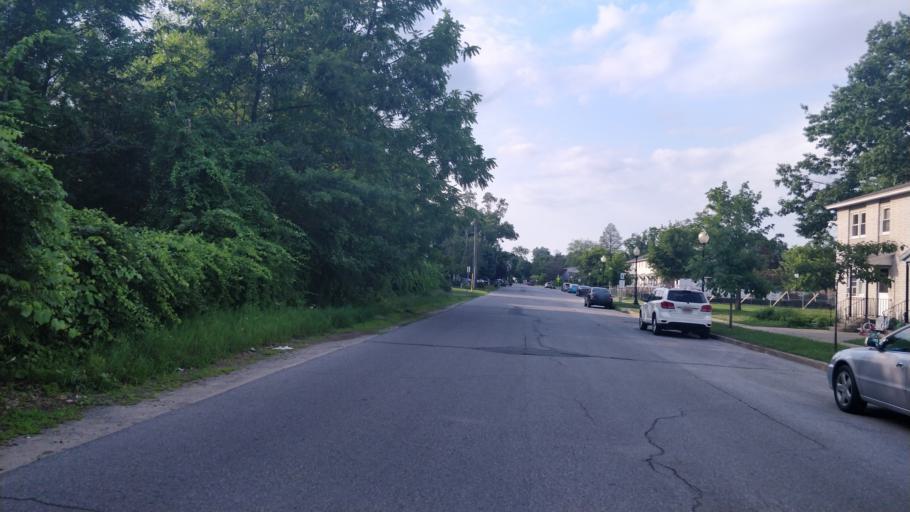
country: US
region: New York
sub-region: Saratoga County
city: Saratoga Springs
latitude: 43.0690
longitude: -73.7825
